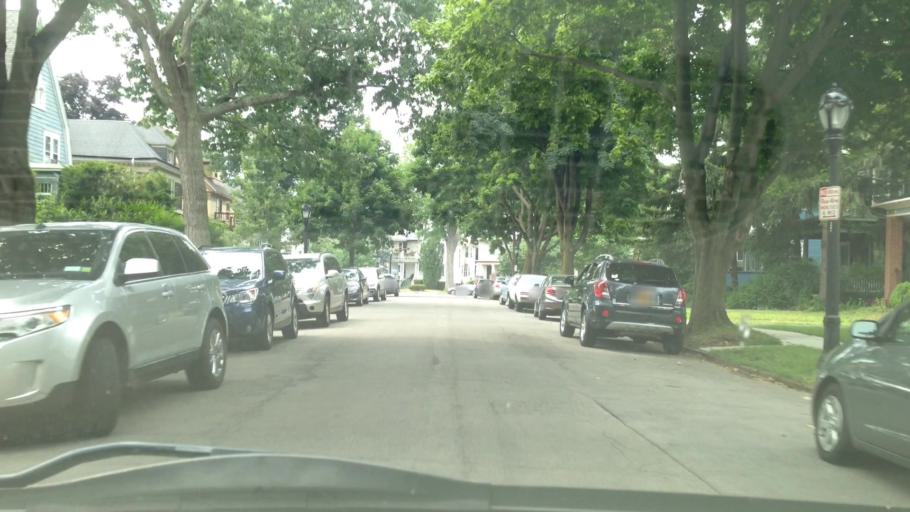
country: US
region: New York
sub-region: Erie County
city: Kenmore
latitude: 42.9345
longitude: -78.8484
